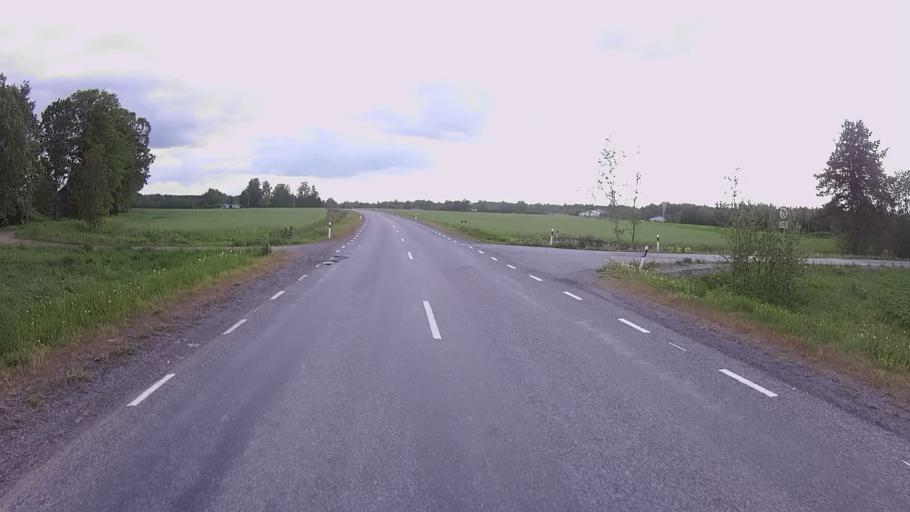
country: EE
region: Jogevamaa
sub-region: Mustvee linn
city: Mustvee
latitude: 59.0032
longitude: 26.9085
